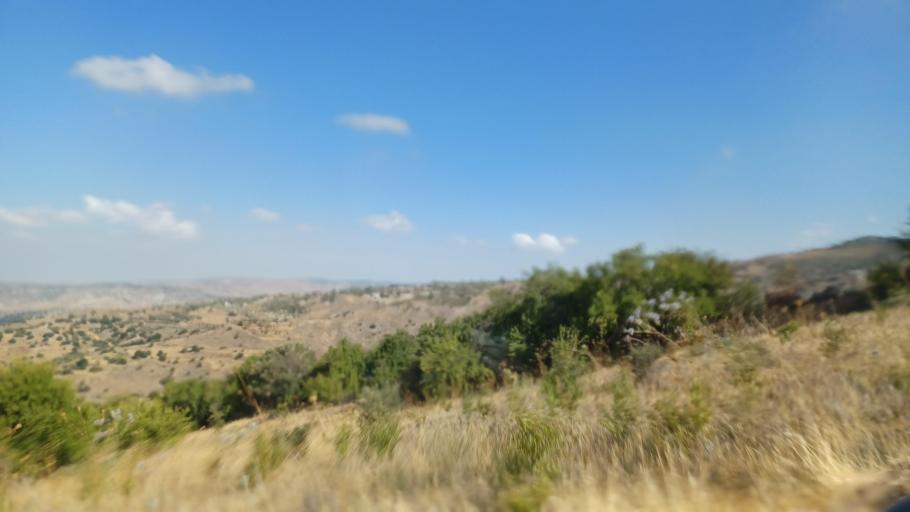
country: CY
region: Pafos
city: Mesogi
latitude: 34.8753
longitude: 32.5965
